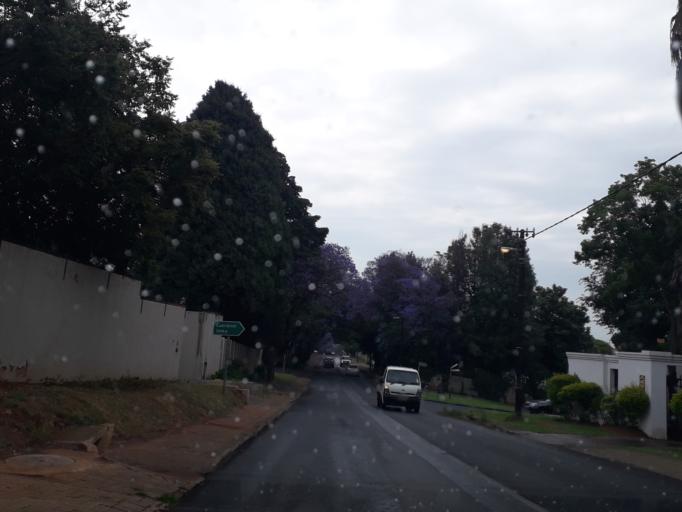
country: ZA
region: Gauteng
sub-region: City of Johannesburg Metropolitan Municipality
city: Johannesburg
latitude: -26.1206
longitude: 27.9978
